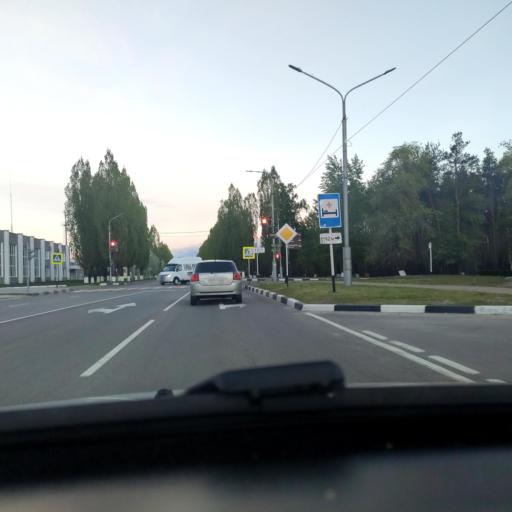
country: RU
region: Voronezj
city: Novovoronezh
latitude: 51.3140
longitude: 39.2189
